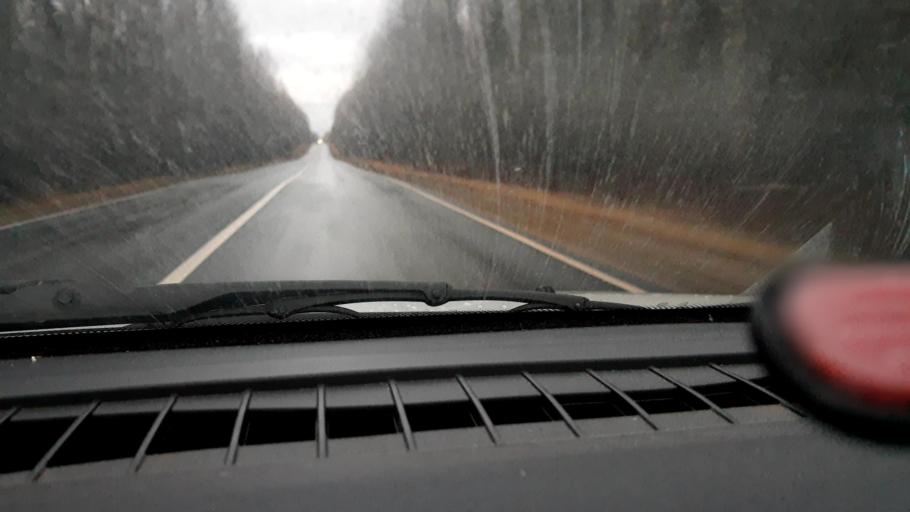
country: RU
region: Nizjnij Novgorod
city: Uren'
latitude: 57.2590
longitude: 45.6133
